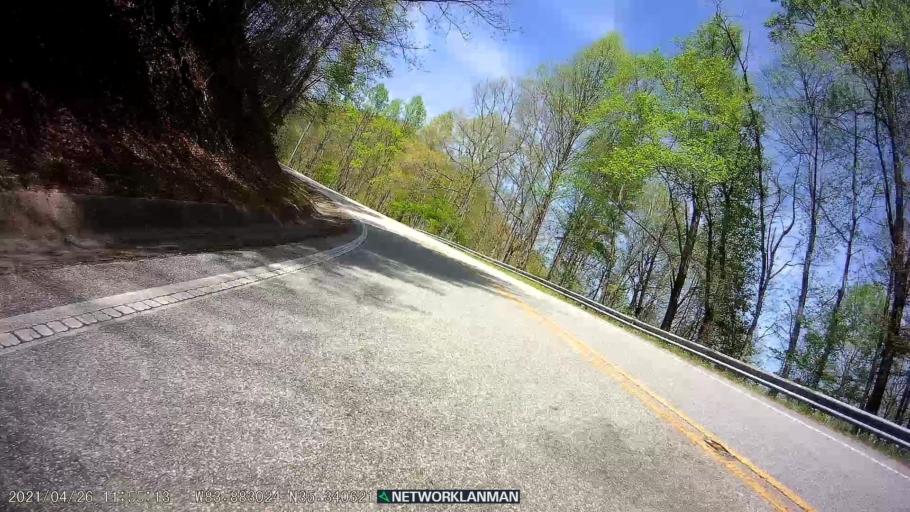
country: US
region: North Carolina
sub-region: Graham County
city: Robbinsville
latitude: 35.3405
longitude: -83.8830
